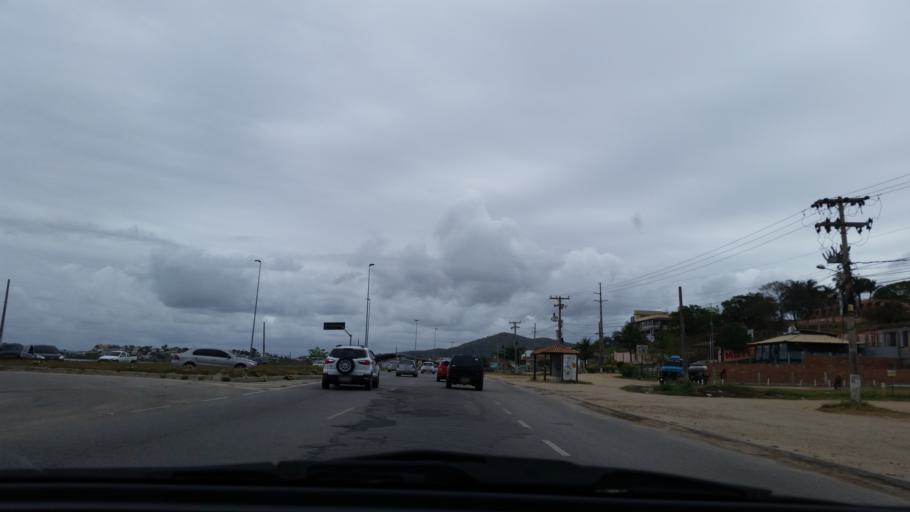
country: BR
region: Rio de Janeiro
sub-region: Sao Pedro Da Aldeia
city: Sao Pedro da Aldeia
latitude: -22.8546
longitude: -42.0609
